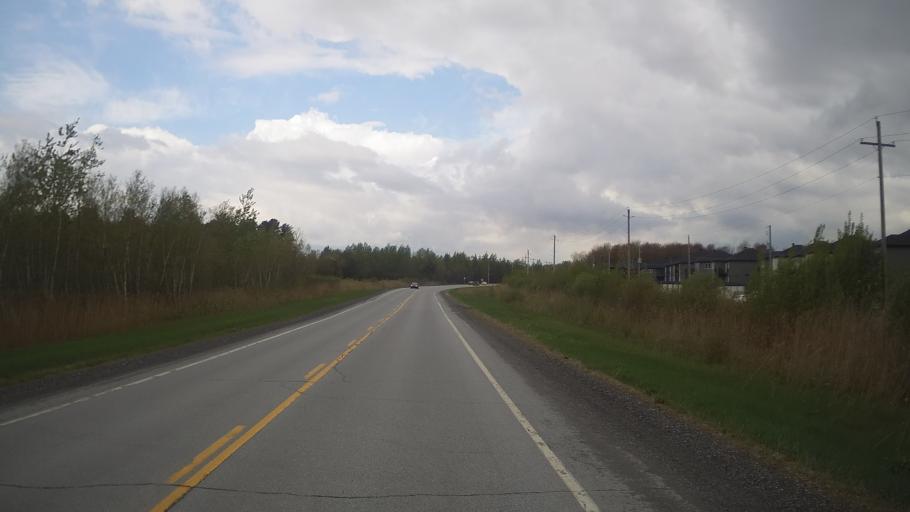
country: CA
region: Quebec
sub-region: Monteregie
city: Farnham
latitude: 45.2706
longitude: -72.9576
